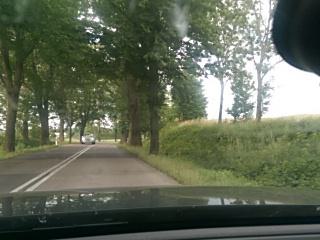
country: PL
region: Warmian-Masurian Voivodeship
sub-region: Powiat gizycki
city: Ryn
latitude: 54.0093
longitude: 21.6418
